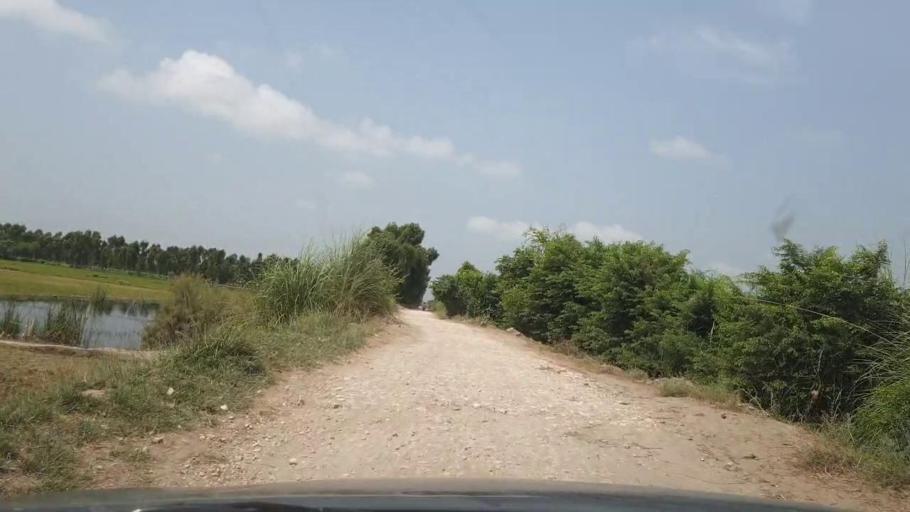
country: PK
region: Sindh
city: Ratodero
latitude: 27.8939
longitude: 68.3102
